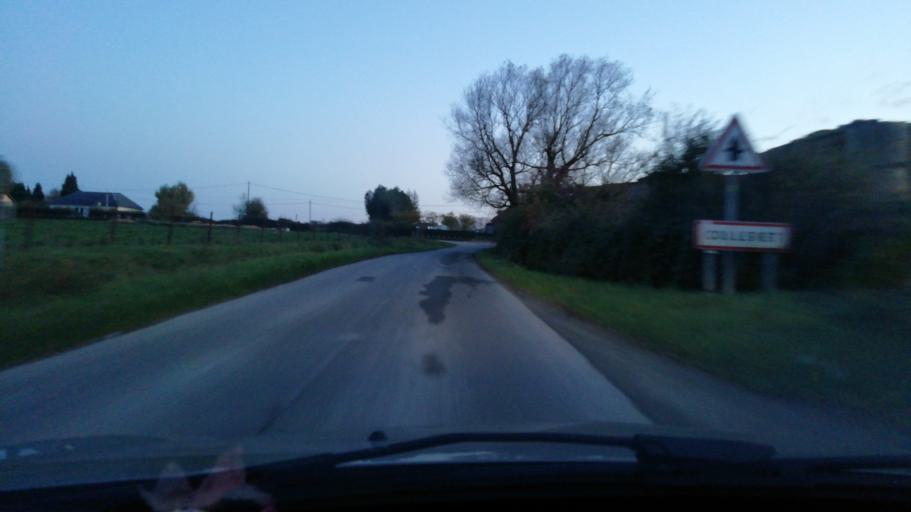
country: FR
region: Nord-Pas-de-Calais
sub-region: Departement du Nord
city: Marpent
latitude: 50.2664
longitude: 4.0873
